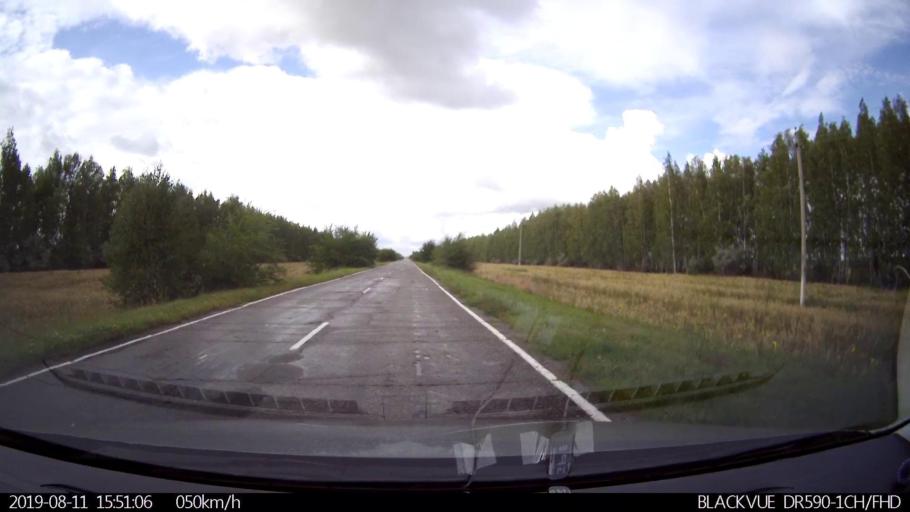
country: RU
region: Ulyanovsk
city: Ignatovka
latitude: 53.9162
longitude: 47.6559
